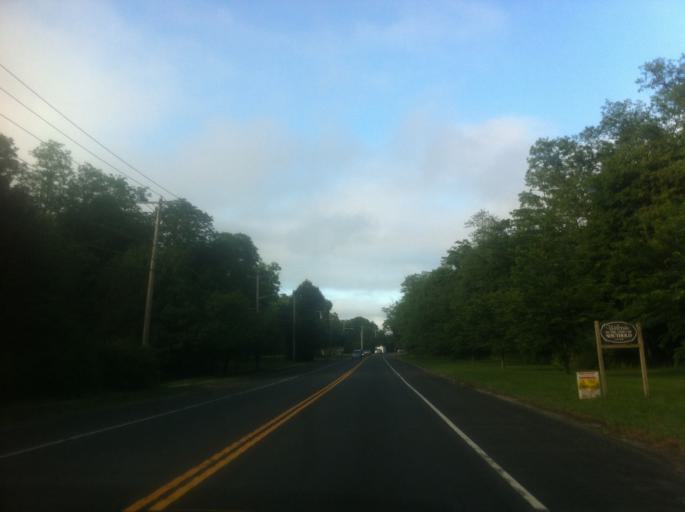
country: US
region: New York
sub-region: Suffolk County
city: Laurel
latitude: 40.9722
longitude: -72.5575
